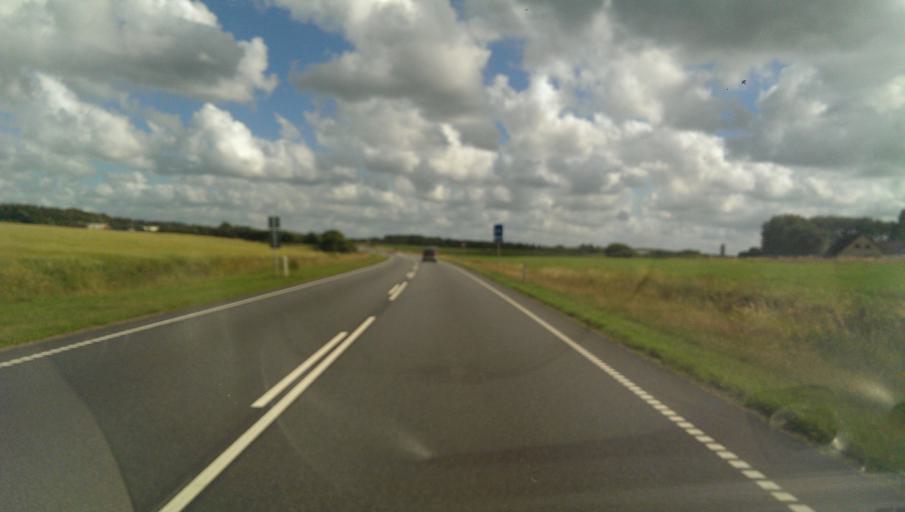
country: DK
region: South Denmark
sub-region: Varde Kommune
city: Varde
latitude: 55.6746
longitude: 8.4917
